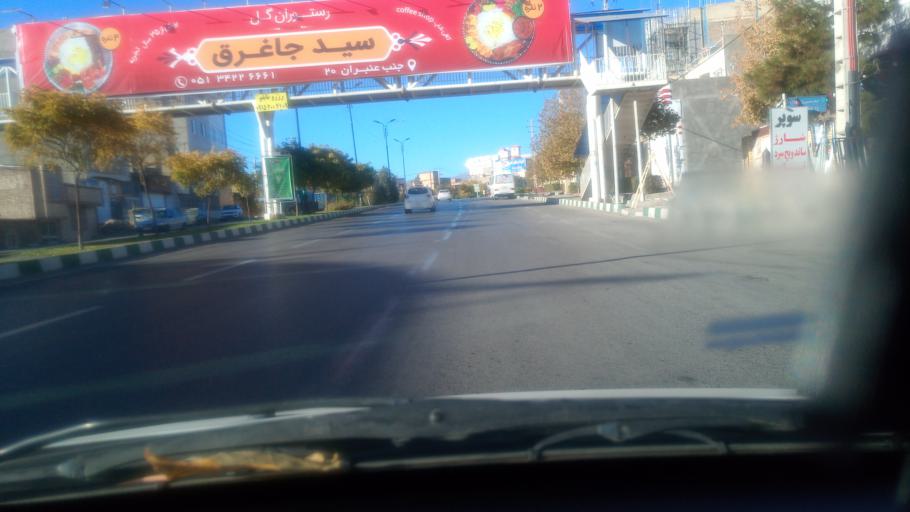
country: IR
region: Razavi Khorasan
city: Torqabeh
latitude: 36.3148
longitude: 59.3778
